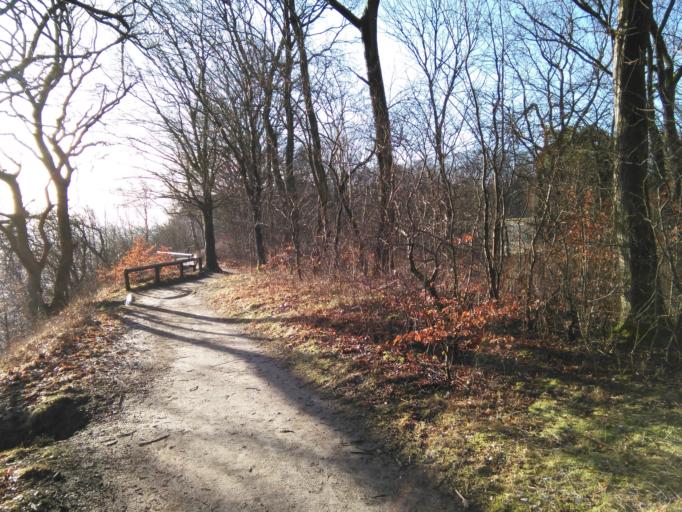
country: DK
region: Central Jutland
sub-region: Arhus Kommune
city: Arhus
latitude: 56.1140
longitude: 10.2300
